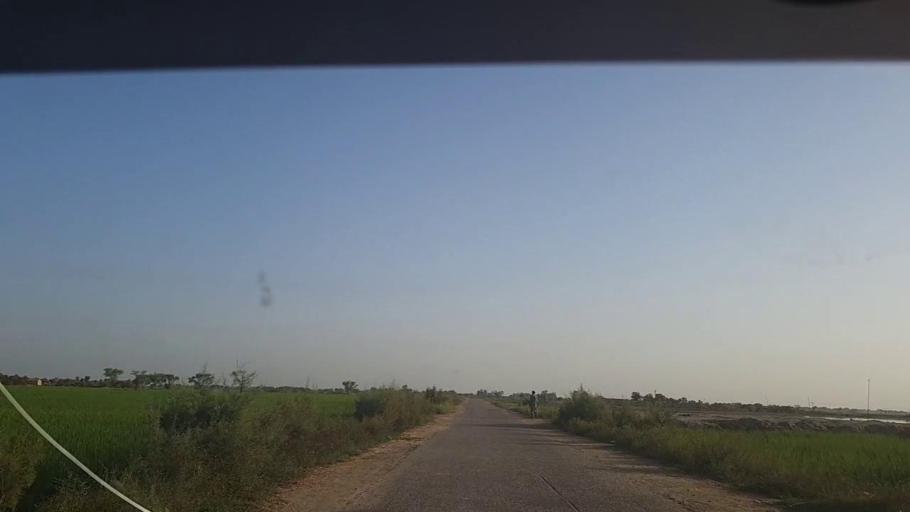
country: PK
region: Sindh
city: Thul
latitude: 28.1952
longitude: 68.8733
